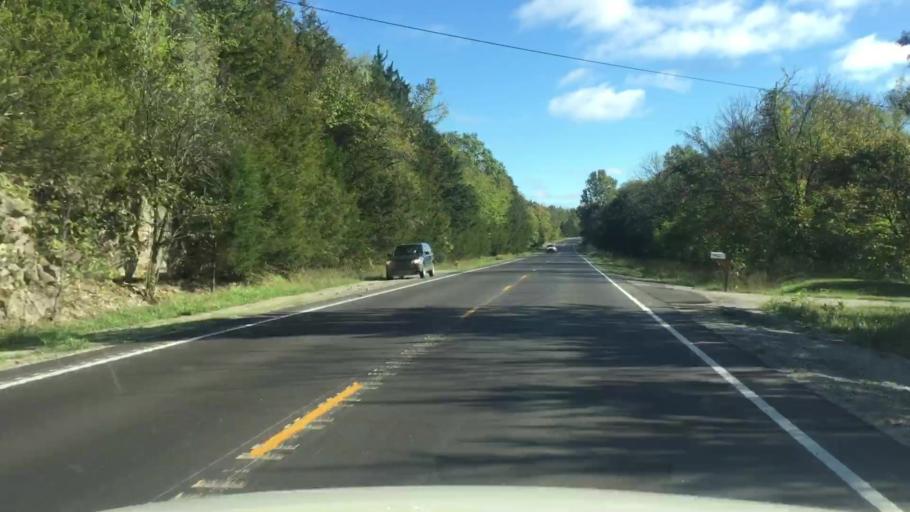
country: US
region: Missouri
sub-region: Howard County
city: New Franklin
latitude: 38.9865
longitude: -92.5382
